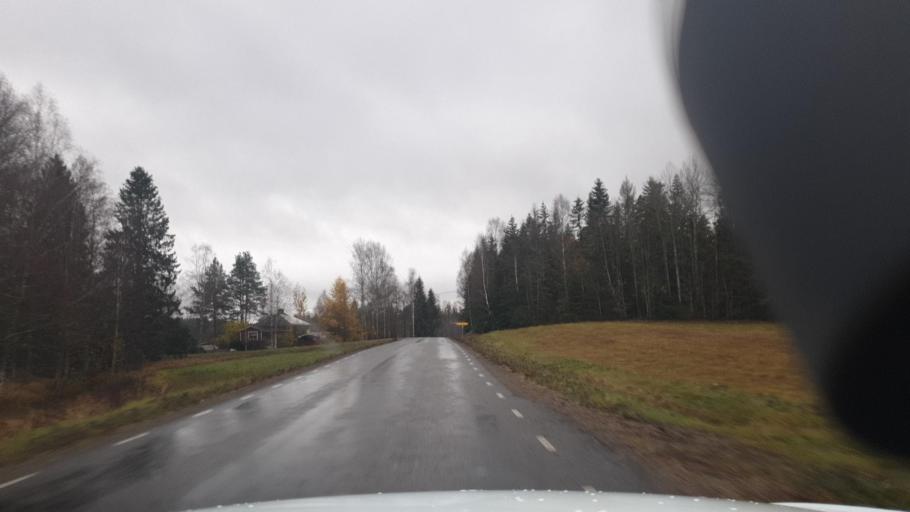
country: SE
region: Vaermland
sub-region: Eda Kommun
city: Charlottenberg
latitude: 59.8032
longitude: 12.1531
